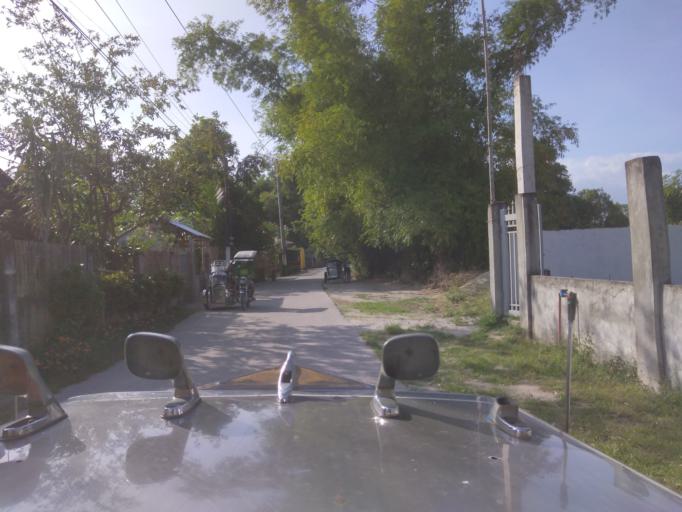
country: PH
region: Central Luzon
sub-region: Province of Pampanga
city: Bulaon
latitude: 15.0930
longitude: 120.6947
